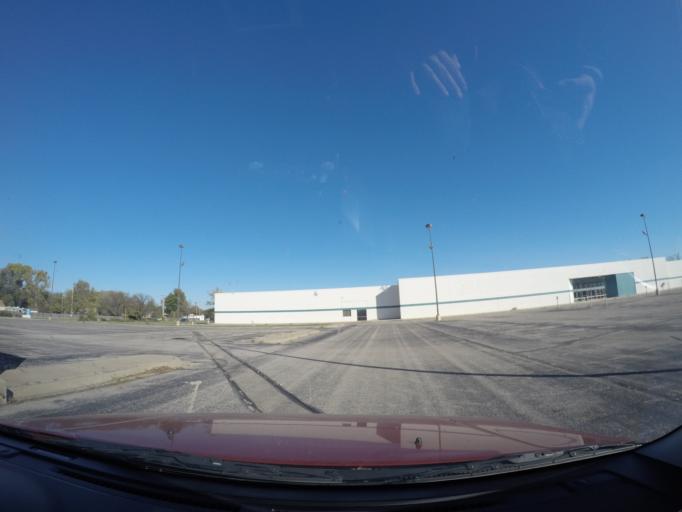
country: US
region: Kansas
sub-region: Sedgwick County
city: Wichita
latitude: 37.6793
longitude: -97.3931
